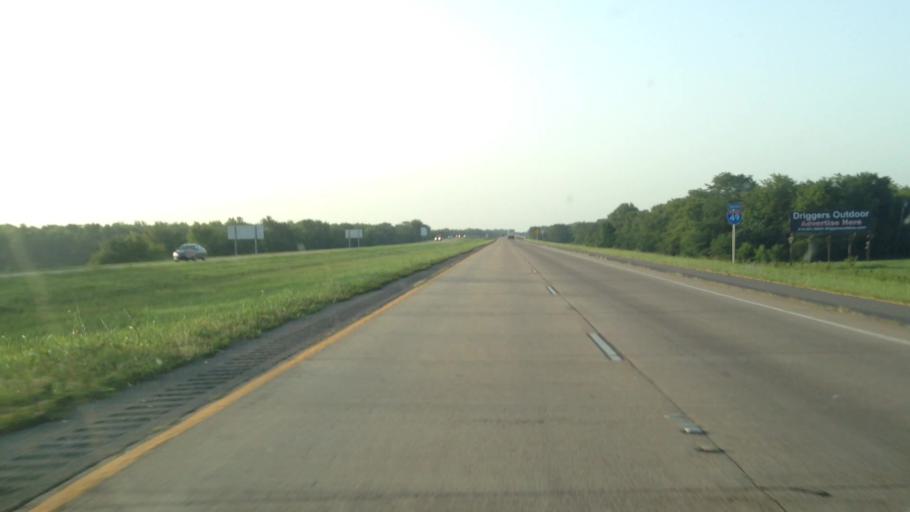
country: US
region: Louisiana
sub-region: Natchitoches Parish
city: Vienna Bend
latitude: 31.6016
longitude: -93.0426
